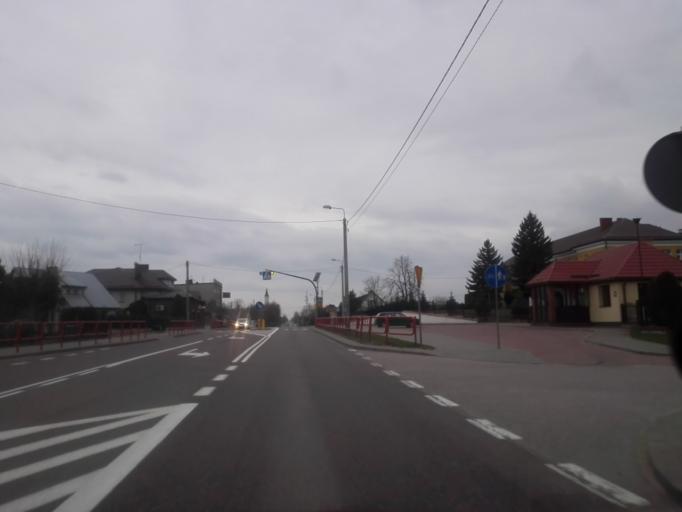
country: PL
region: Podlasie
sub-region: Powiat grajewski
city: Rajgrod
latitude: 53.7750
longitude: 22.8267
